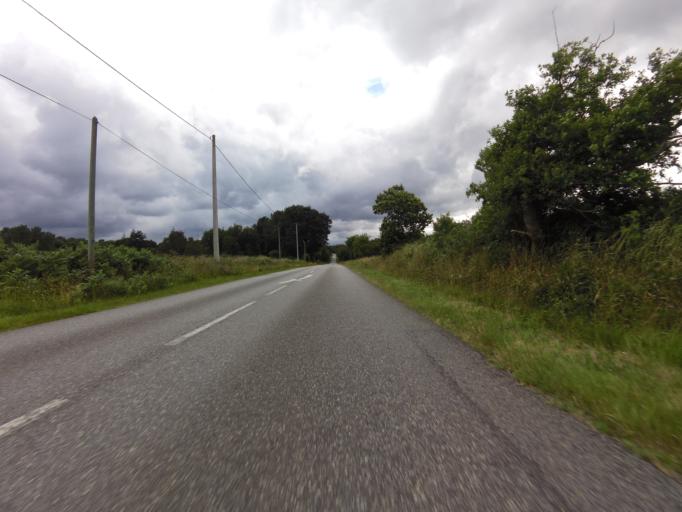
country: FR
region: Brittany
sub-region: Departement du Morbihan
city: Saint-Martin-sur-Oust
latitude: 47.7265
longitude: -2.2983
